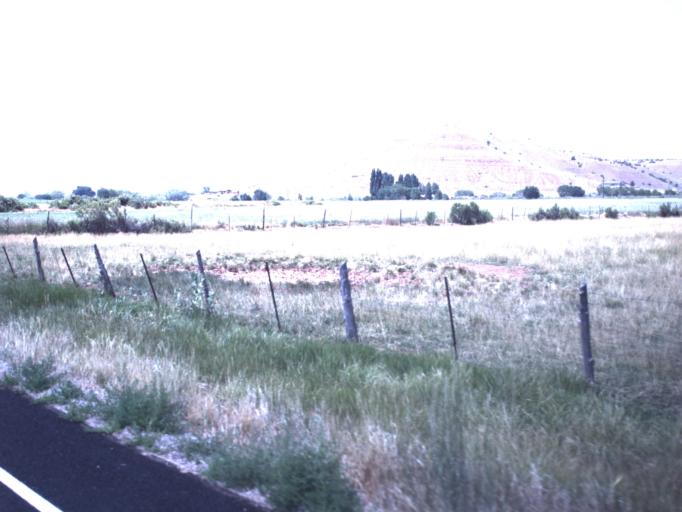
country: US
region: Utah
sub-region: Uintah County
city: Maeser
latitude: 40.4038
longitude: -109.7787
